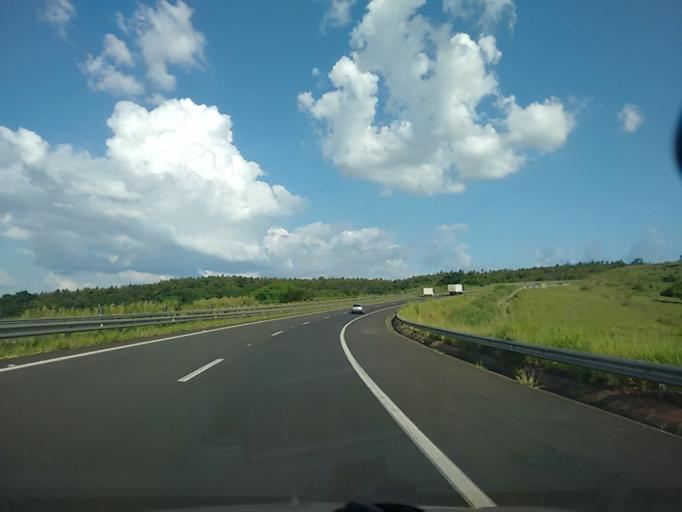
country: BR
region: Sao Paulo
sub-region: Duartina
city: Duartina
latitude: -22.3201
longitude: -49.4794
